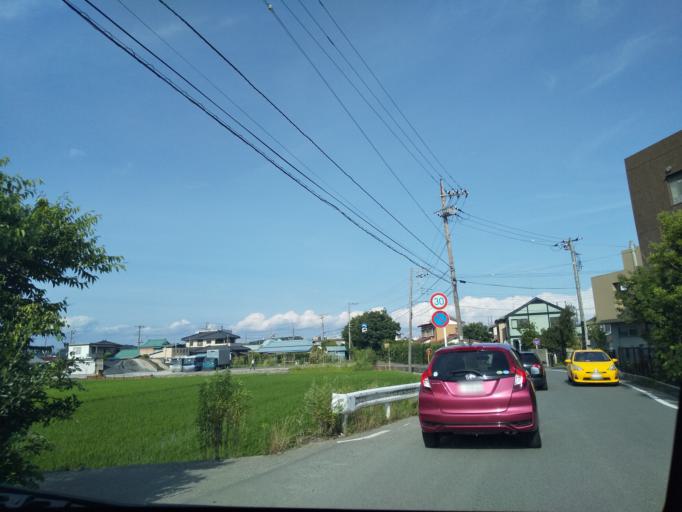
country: JP
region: Kanagawa
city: Zama
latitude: 35.4800
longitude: 139.3801
